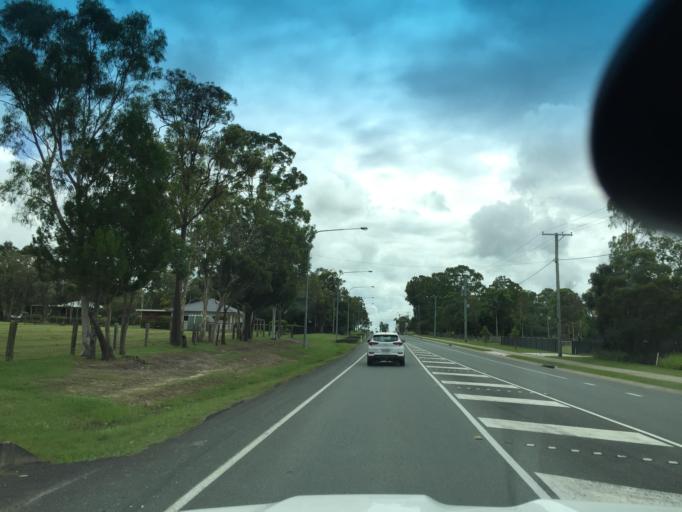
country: AU
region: Queensland
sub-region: Moreton Bay
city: Burpengary
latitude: -27.1427
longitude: 152.9807
